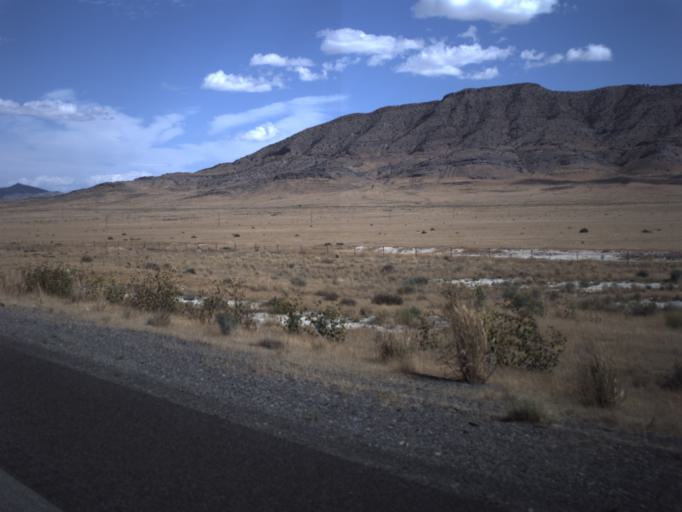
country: US
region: Utah
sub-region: Tooele County
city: Grantsville
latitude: 40.7810
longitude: -112.9672
